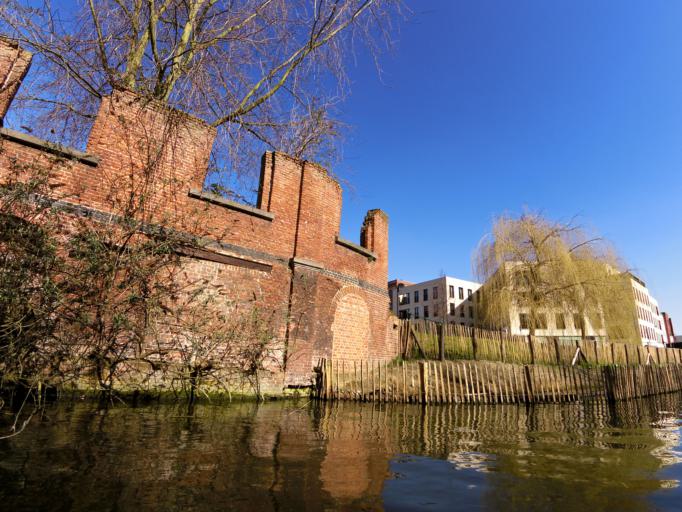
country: BE
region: Flanders
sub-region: Provincie Oost-Vlaanderen
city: Gent
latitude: 51.0602
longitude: 3.7144
